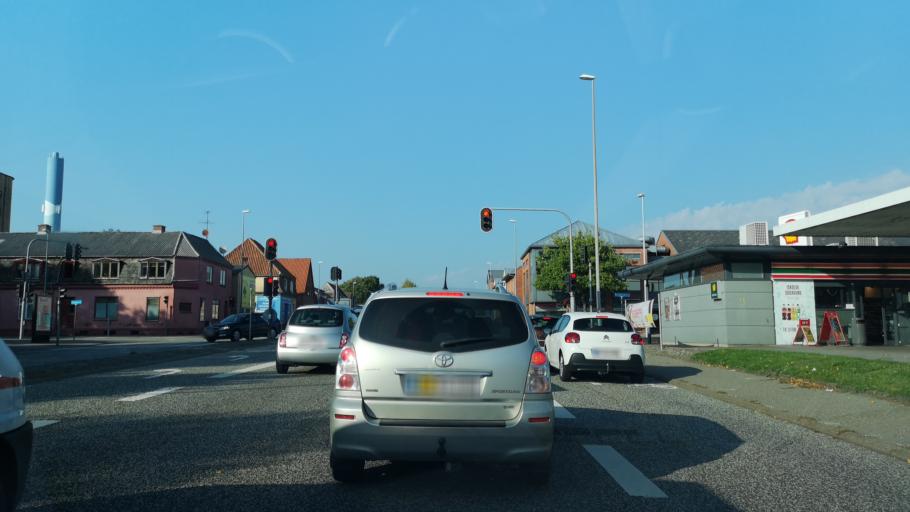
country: DK
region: Central Jutland
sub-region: Herning Kommune
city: Herning
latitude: 56.1378
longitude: 8.9675
